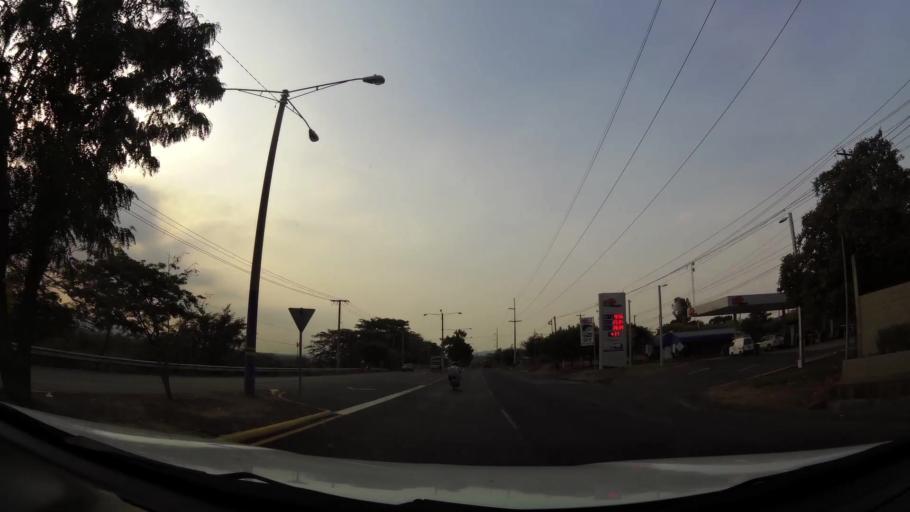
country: NI
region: Managua
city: Ciudad Sandino
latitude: 12.1592
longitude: -86.3387
